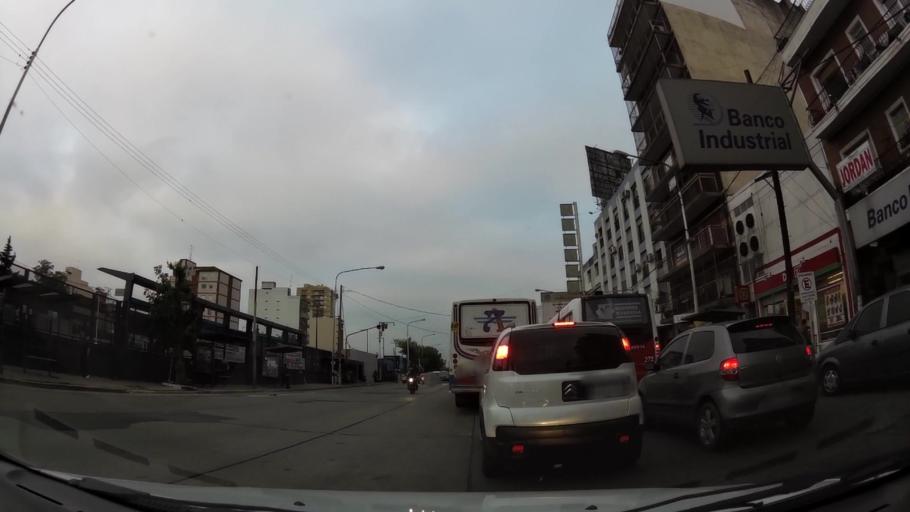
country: AR
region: Buenos Aires
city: San Justo
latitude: -34.6402
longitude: -58.5420
